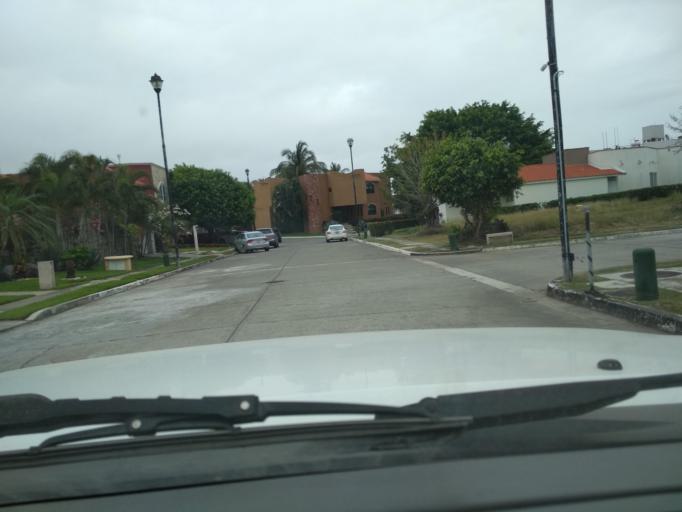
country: MX
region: Veracruz
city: Boca del Rio
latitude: 19.0909
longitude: -96.1152
